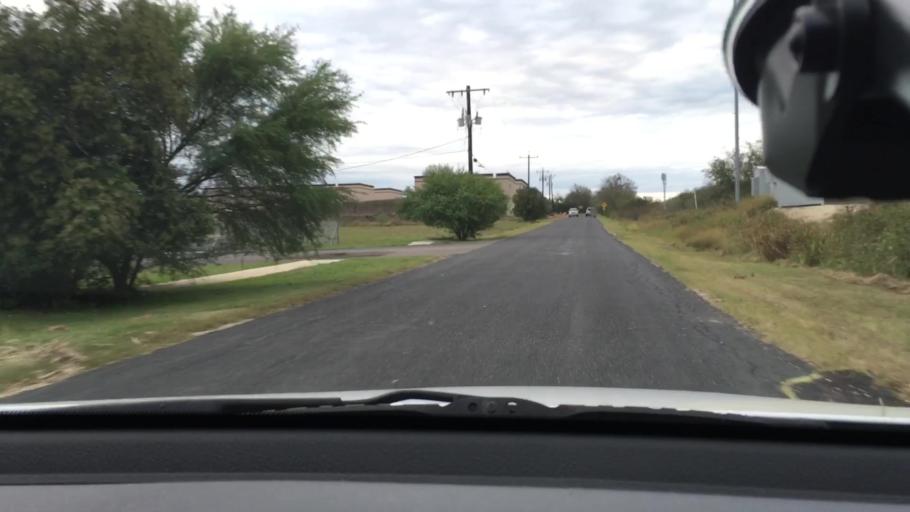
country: US
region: Texas
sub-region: Bexar County
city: Converse
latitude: 29.5239
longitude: -98.3099
